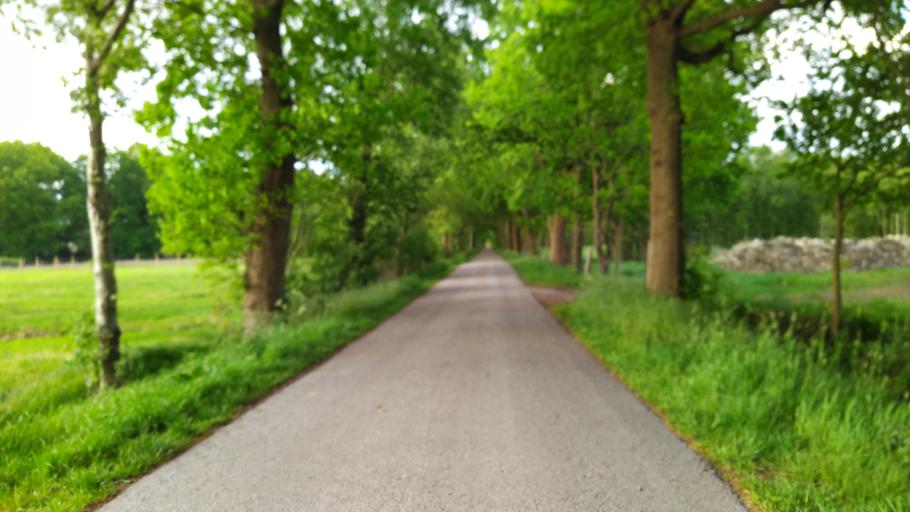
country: DE
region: Lower Saxony
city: Bargstedt
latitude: 53.4823
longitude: 9.4297
